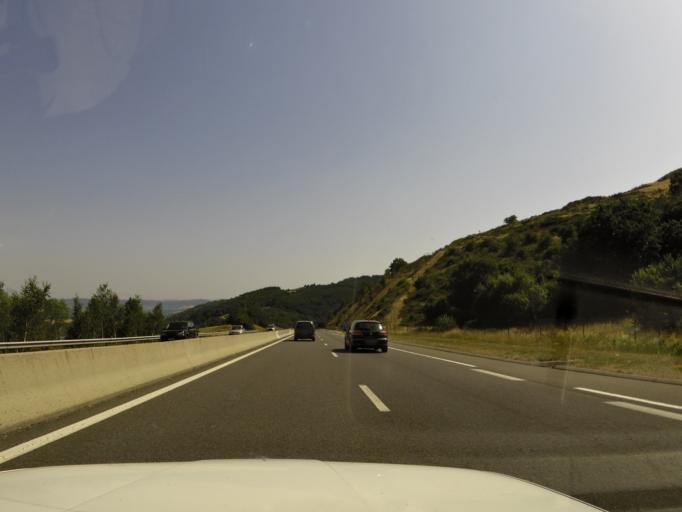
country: FR
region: Languedoc-Roussillon
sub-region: Departement de la Lozere
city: Marvejols
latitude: 44.5788
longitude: 3.2492
